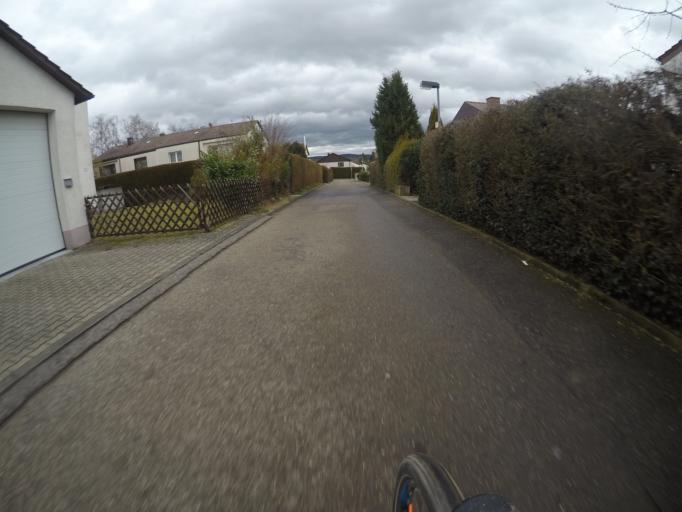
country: DE
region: Baden-Wuerttemberg
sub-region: Regierungsbezirk Stuttgart
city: Herrenberg
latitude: 48.5951
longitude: 8.8479
